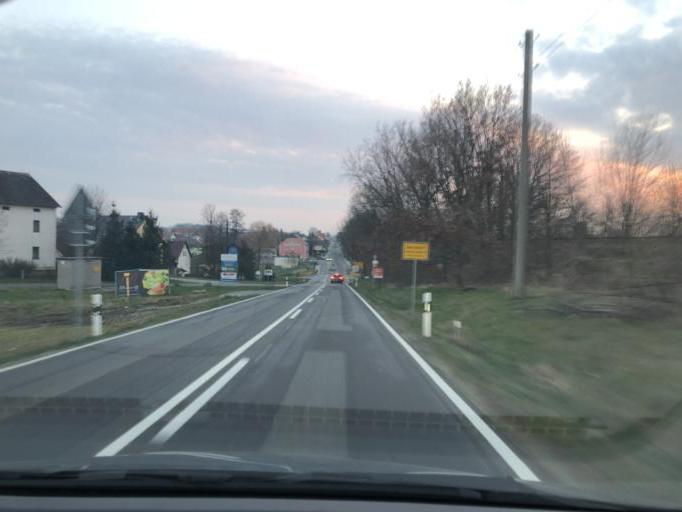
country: DE
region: Saxony
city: Haselbachtal
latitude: 51.2335
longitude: 14.0506
